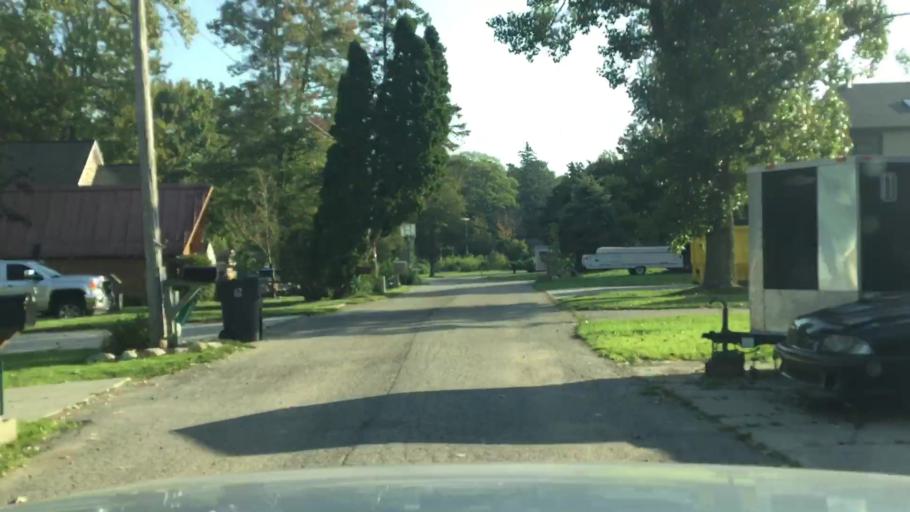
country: US
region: Michigan
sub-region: Livingston County
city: Whitmore Lake
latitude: 42.4434
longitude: -83.8358
